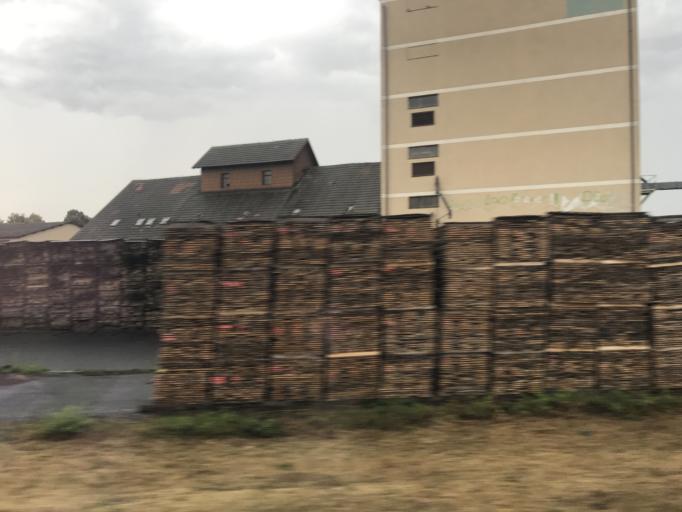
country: DE
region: Bavaria
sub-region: Regierungsbezirk Unterfranken
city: Bergtheim
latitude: 49.9010
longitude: 10.0764
